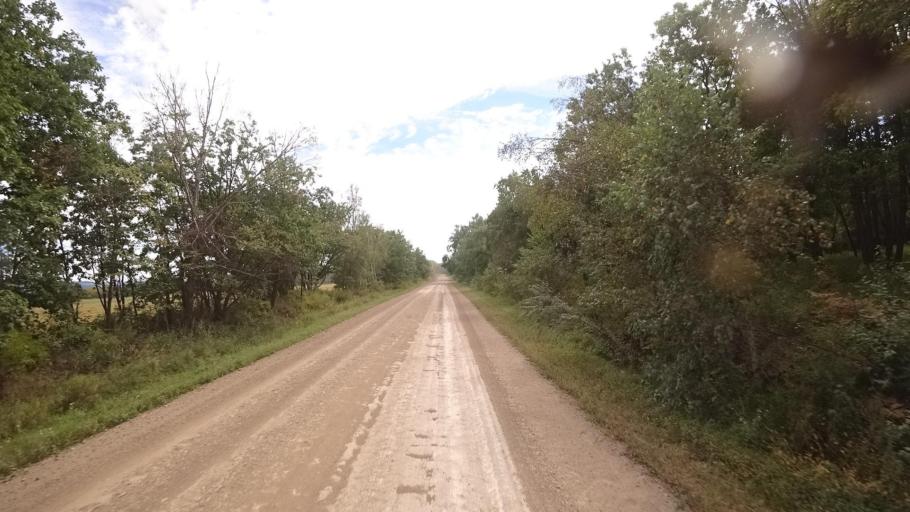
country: RU
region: Primorskiy
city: Yakovlevka
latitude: 44.5179
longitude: 133.5971
